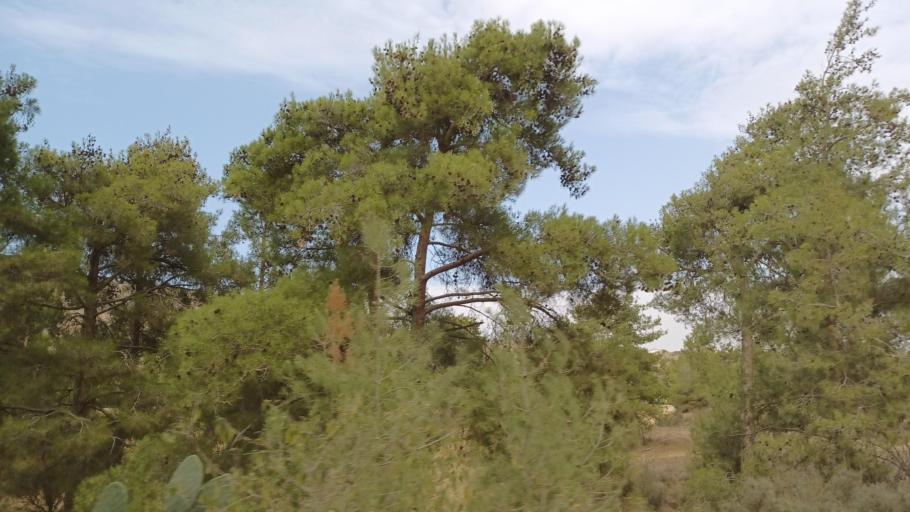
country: CY
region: Lefkosia
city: Klirou
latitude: 35.0411
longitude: 33.1143
